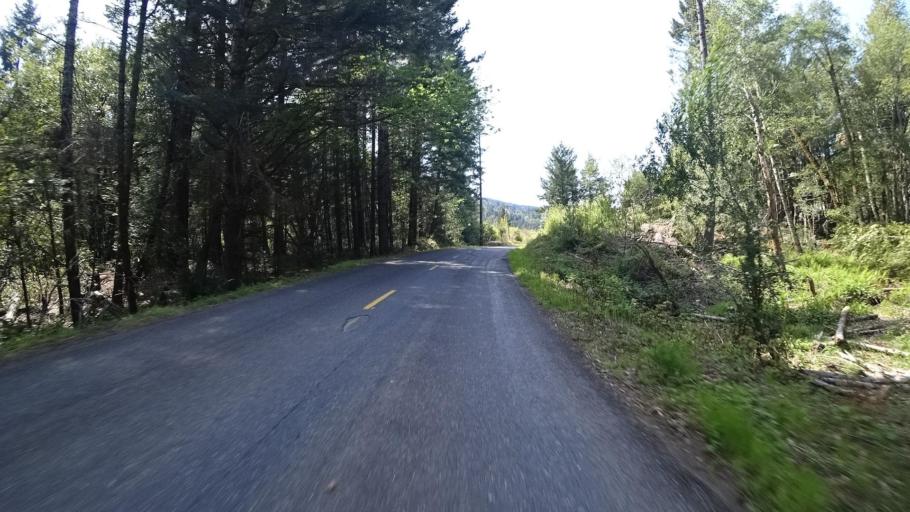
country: US
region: California
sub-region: Humboldt County
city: Redway
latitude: 40.3390
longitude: -123.6976
